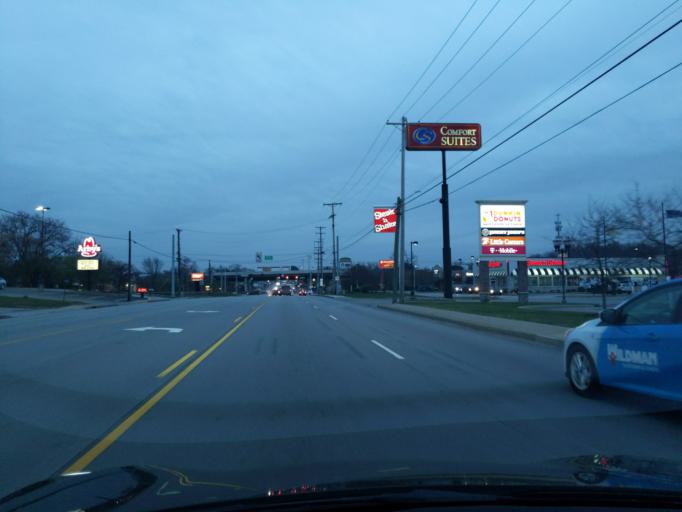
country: US
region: Indiana
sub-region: Saint Joseph County
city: Georgetown
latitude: 41.7231
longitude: -86.2504
